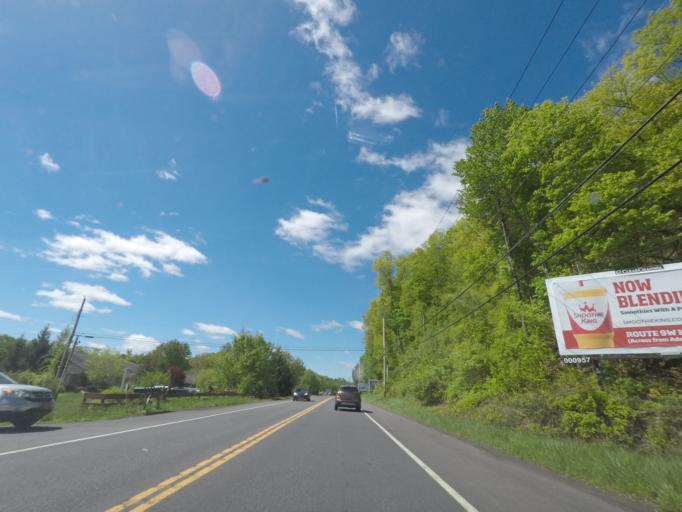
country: US
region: New York
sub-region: Ulster County
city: Glasco
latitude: 42.0456
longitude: -73.9625
